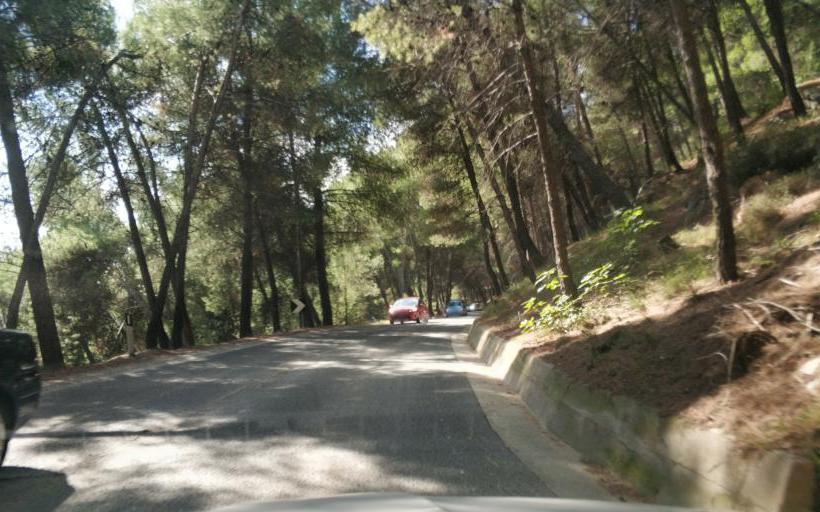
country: AL
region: Durres
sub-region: Rrethi i Krujes
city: Kruje
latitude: 41.4958
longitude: 19.7751
